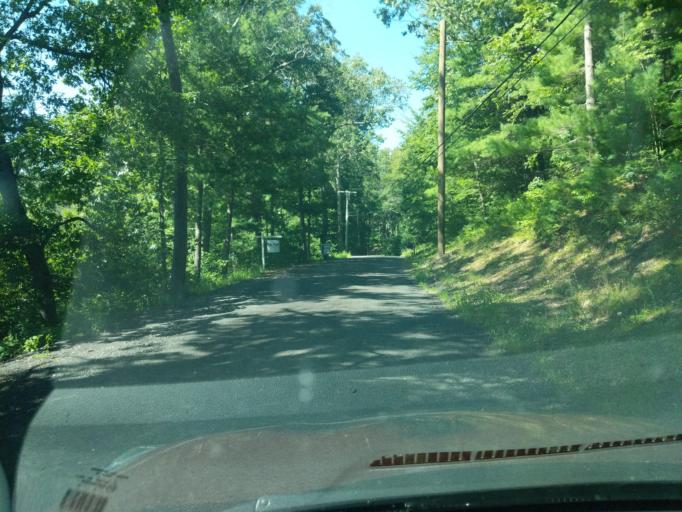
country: US
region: Connecticut
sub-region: Tolland County
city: Crystal Lake
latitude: 41.9263
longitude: -72.3533
